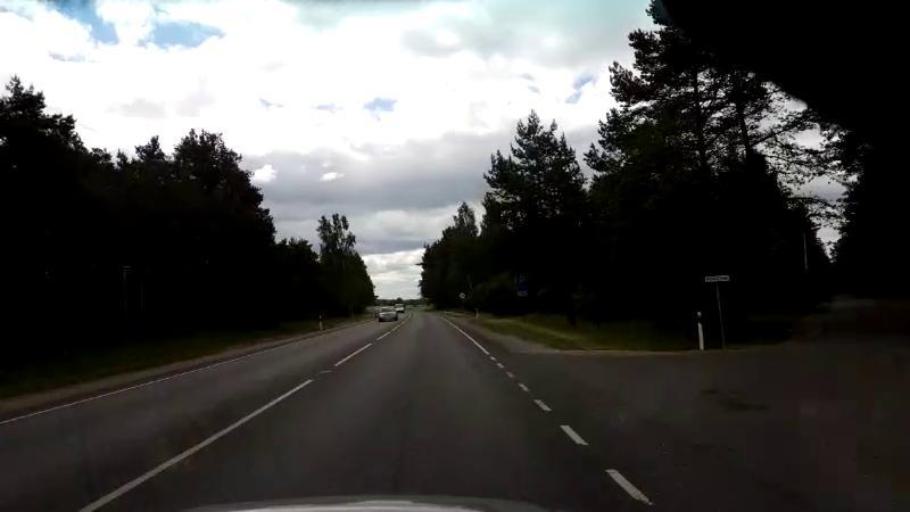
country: EE
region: Paernumaa
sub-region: Paikuse vald
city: Paikuse
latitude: 58.3157
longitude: 24.6018
